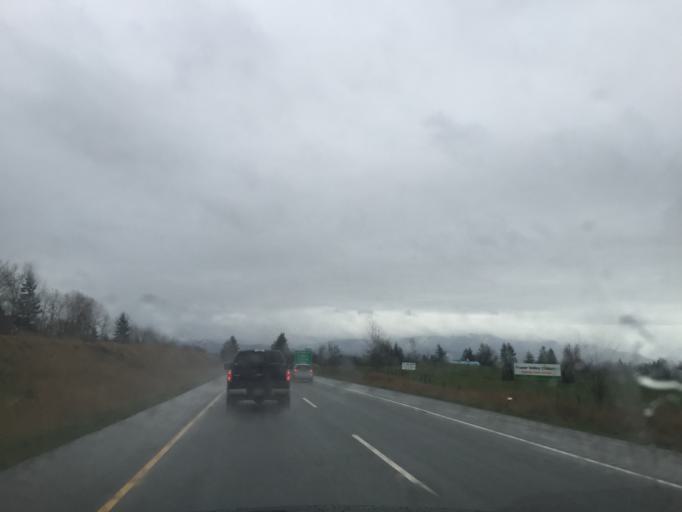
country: CA
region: British Columbia
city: Aldergrove
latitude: 49.0660
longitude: -122.4031
